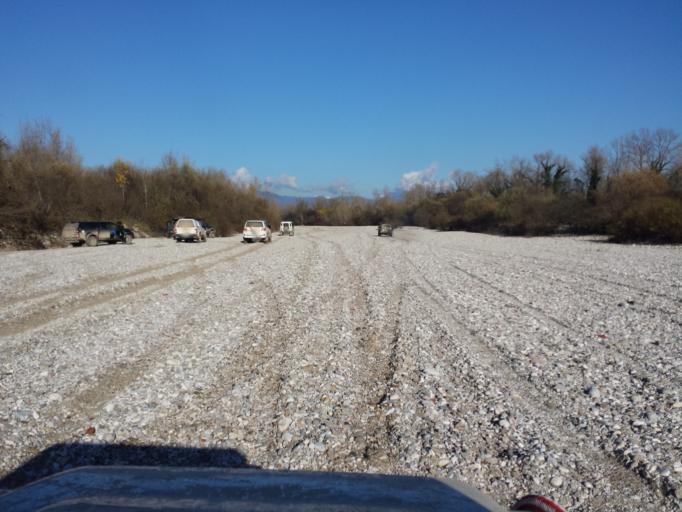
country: IT
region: Friuli Venezia Giulia
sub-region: Provincia di Udine
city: Pradamano
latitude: 46.0243
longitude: 13.3127
